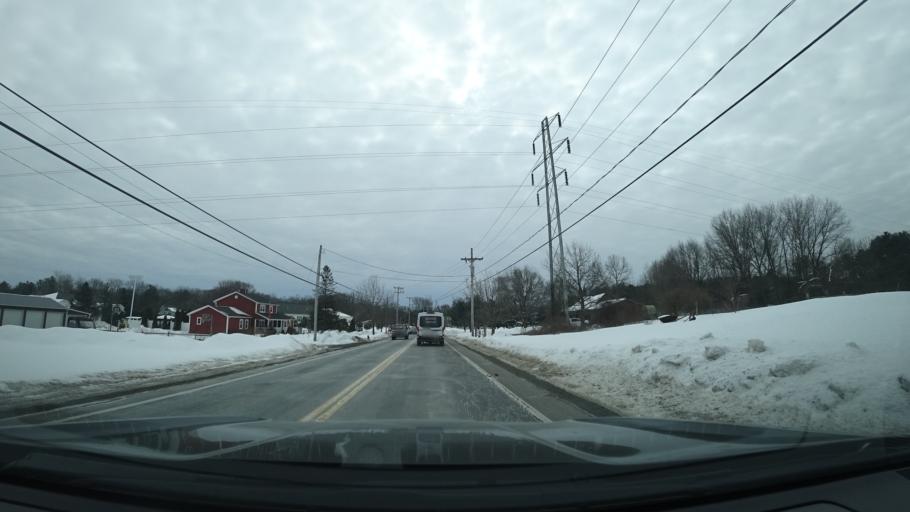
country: US
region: New York
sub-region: Saratoga County
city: South Glens Falls
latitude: 43.2859
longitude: -73.6229
